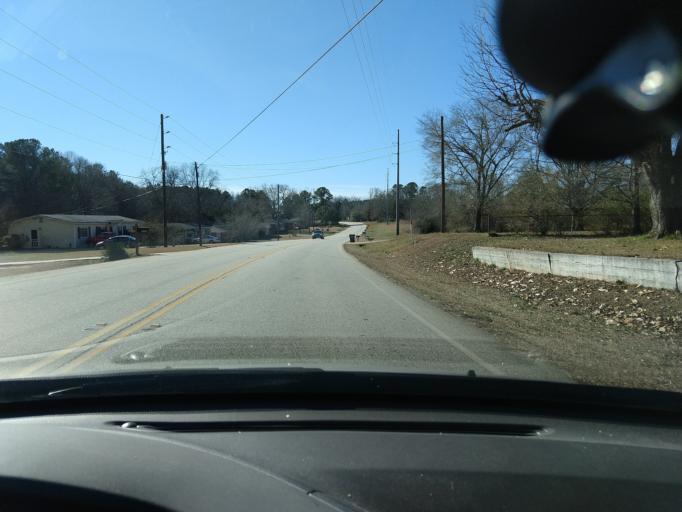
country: US
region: Georgia
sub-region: Walton County
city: Social Circle
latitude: 33.5119
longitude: -83.7331
